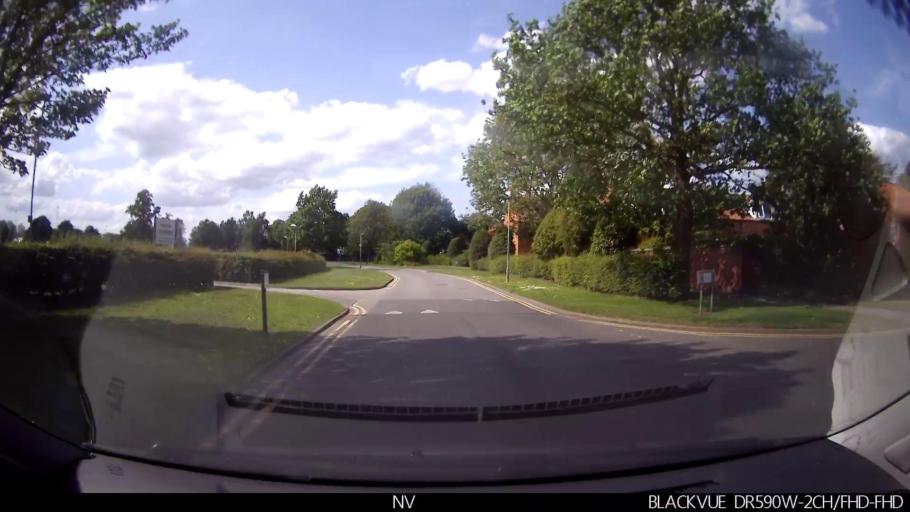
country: GB
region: England
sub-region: City of York
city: Heslington
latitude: 53.9424
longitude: -1.0504
